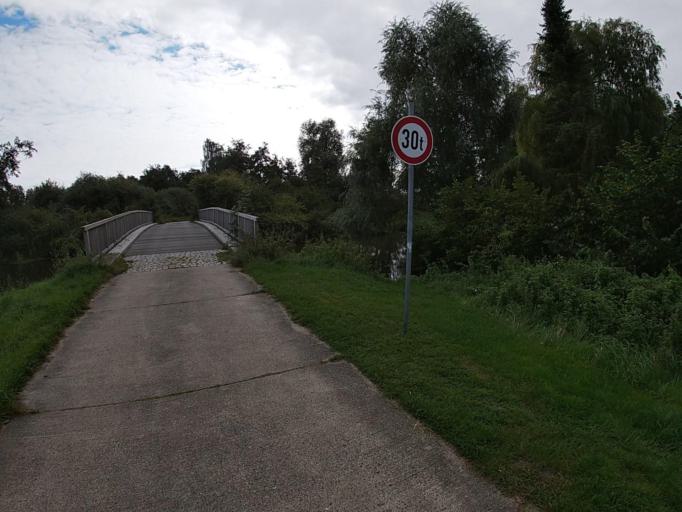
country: DE
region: Lower Saxony
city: Artlenburg
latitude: 53.3323
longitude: 10.4910
